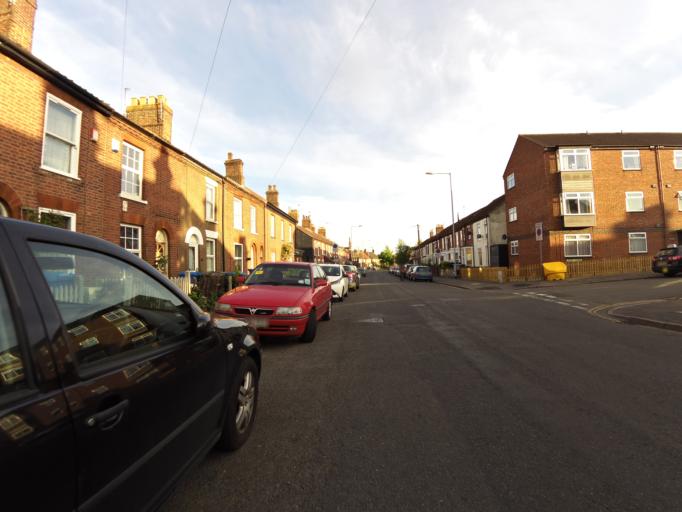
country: GB
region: England
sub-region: Norfolk
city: Norwich
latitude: 52.6421
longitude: 1.2928
